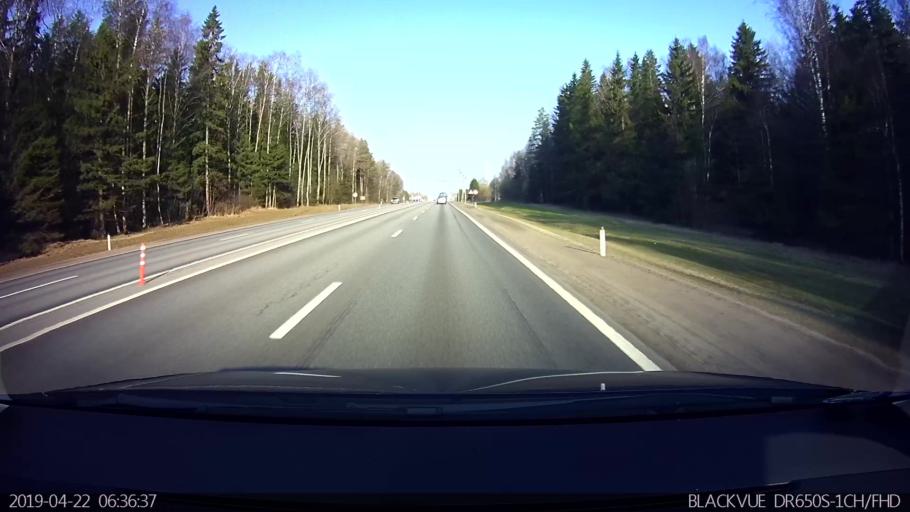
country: RU
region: Moskovskaya
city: Uvarovka
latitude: 55.4858
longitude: 35.4236
